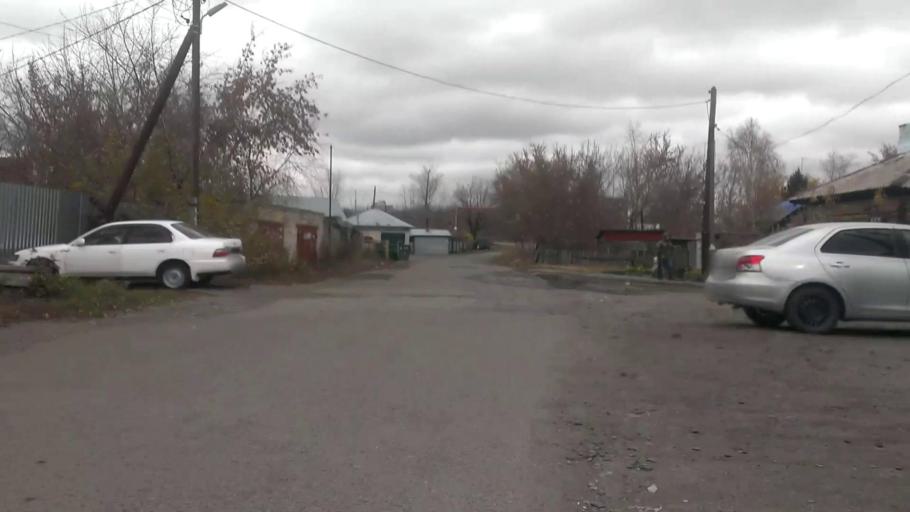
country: RU
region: Altai Krai
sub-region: Gorod Barnaulskiy
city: Barnaul
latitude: 53.3532
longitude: 83.7536
